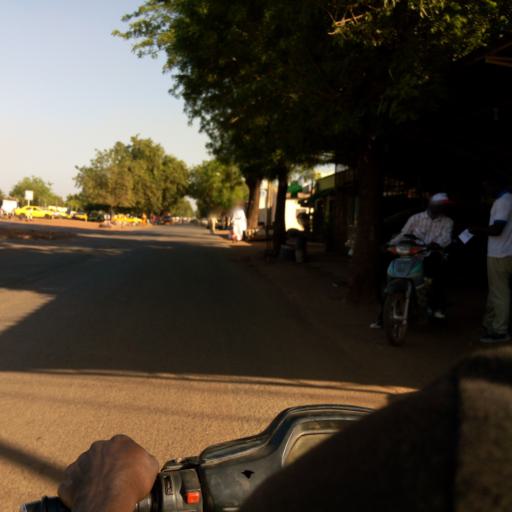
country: ML
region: Bamako
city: Bamako
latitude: 12.6565
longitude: -8.0270
